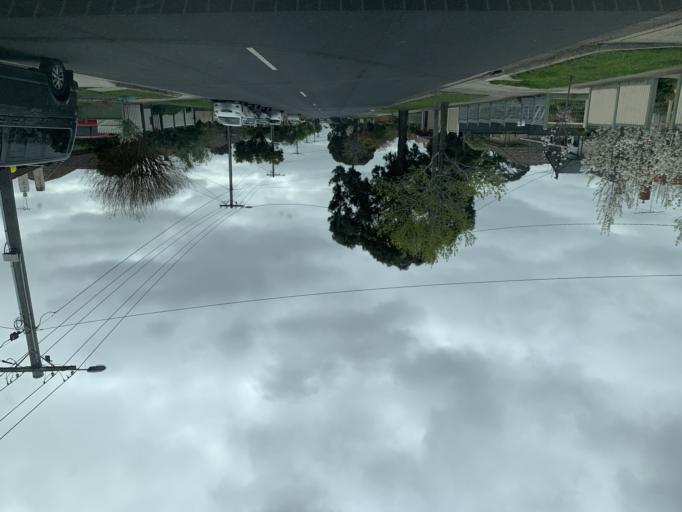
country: AU
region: Victoria
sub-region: Moreland
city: Pascoe Vale South
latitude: -37.7425
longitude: 144.9396
